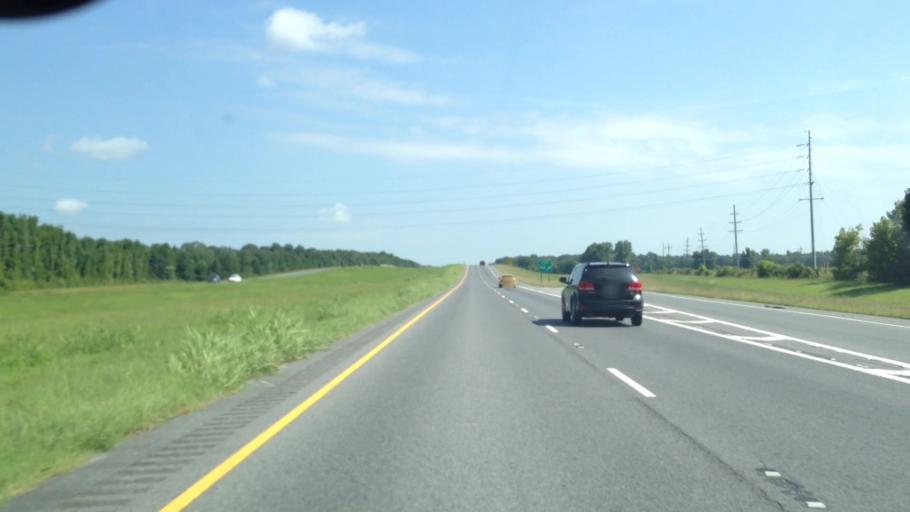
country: US
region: Louisiana
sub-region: Avoyelles Parish
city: Bunkie
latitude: 30.8610
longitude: -92.2280
